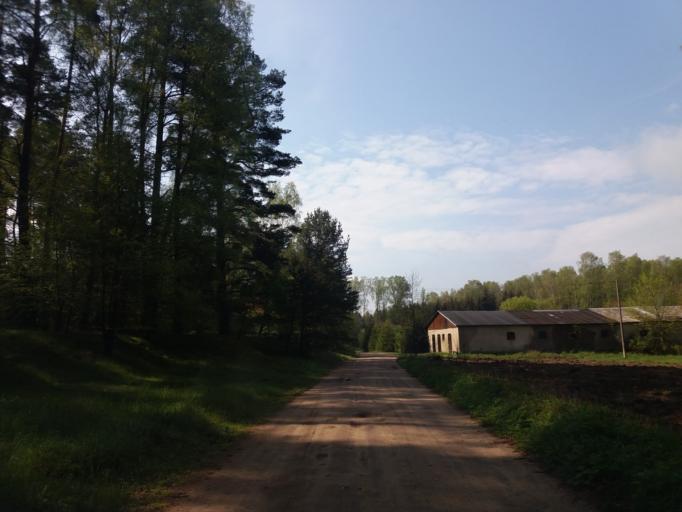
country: PL
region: West Pomeranian Voivodeship
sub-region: Powiat choszczenski
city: Drawno
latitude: 53.2310
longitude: 15.8190
